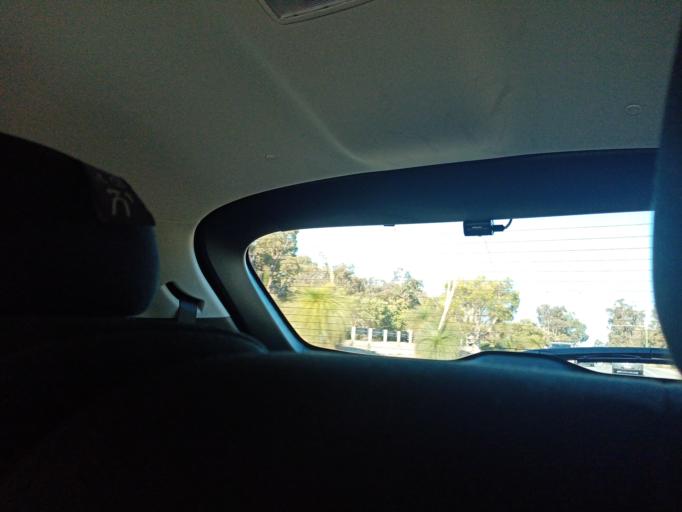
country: AU
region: Western Australia
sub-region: City of Cockburn
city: Yangebup
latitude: -32.1278
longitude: 115.8259
